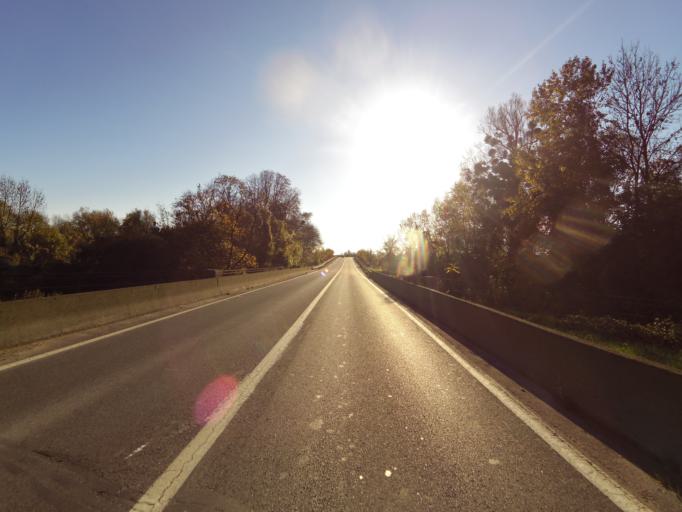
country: FR
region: Champagne-Ardenne
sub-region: Departement de l'Aube
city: Breviandes
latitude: 48.2523
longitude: 4.1094
